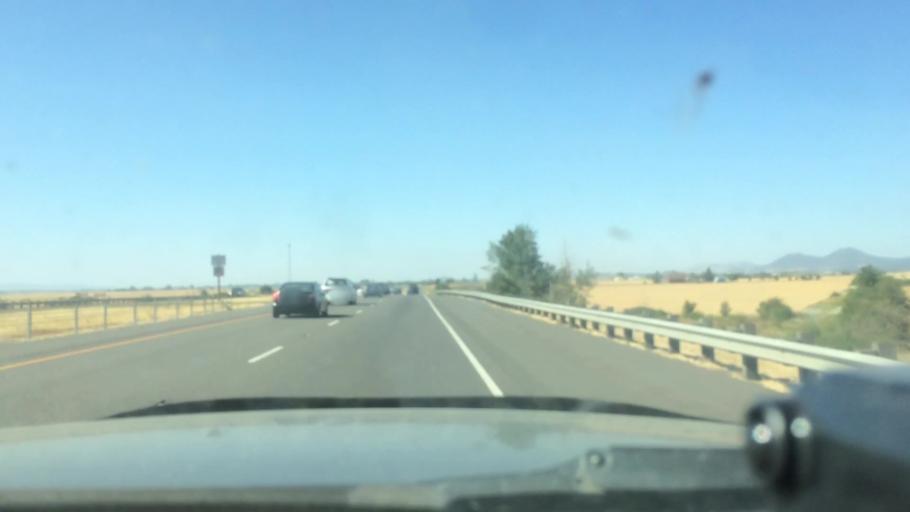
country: US
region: Oregon
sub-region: Linn County
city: Brownsville
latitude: 44.3153
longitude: -123.0609
